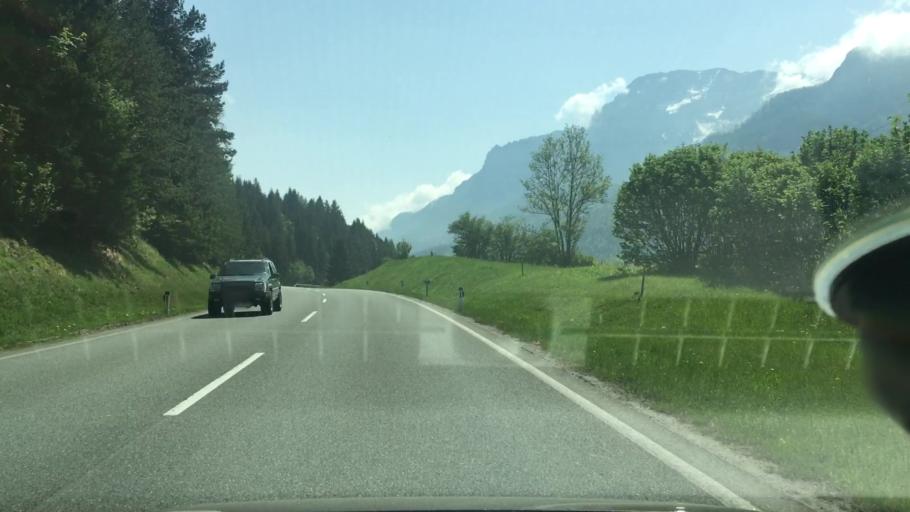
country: AT
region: Tyrol
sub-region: Politischer Bezirk Kitzbuhel
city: Waidring
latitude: 47.5883
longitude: 12.5685
